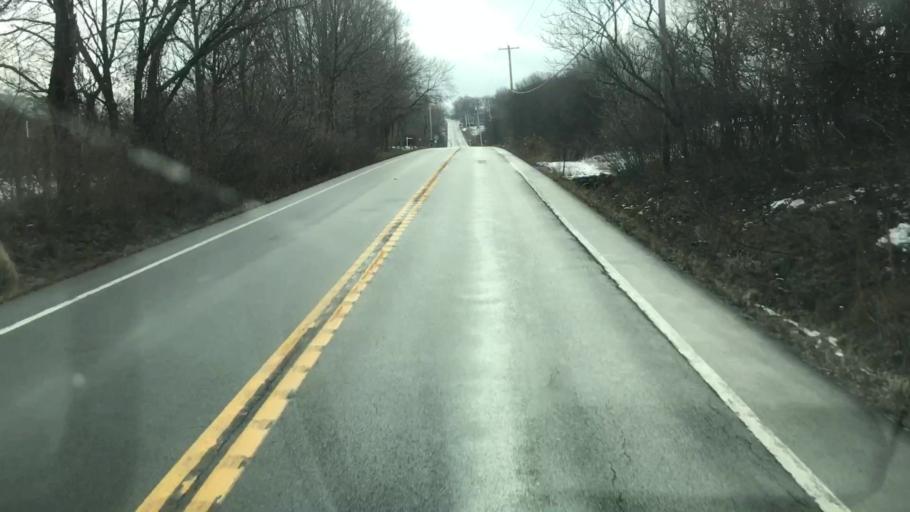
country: US
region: New York
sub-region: Onondaga County
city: Skaneateles
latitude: 42.8542
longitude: -76.3956
